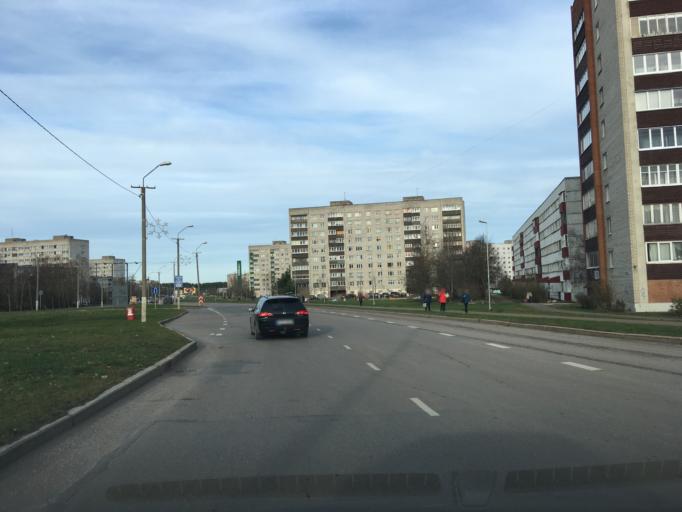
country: EE
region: Ida-Virumaa
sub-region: Narva linn
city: Narva
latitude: 59.3827
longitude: 28.1799
